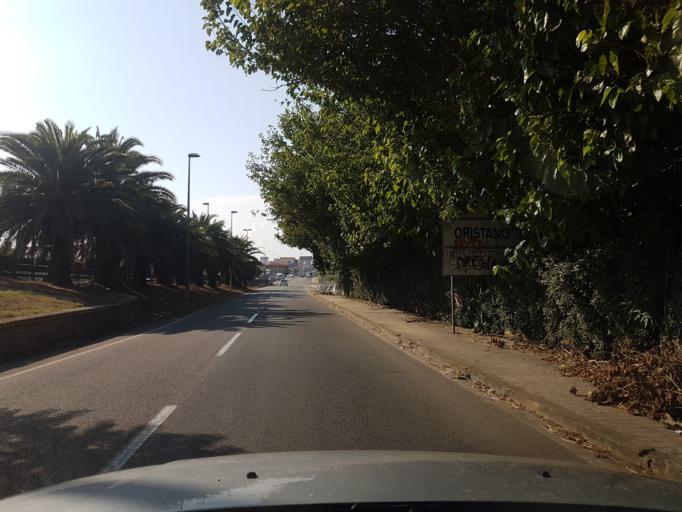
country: IT
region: Sardinia
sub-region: Provincia di Oristano
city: Oristano
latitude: 39.9171
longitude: 8.5840
